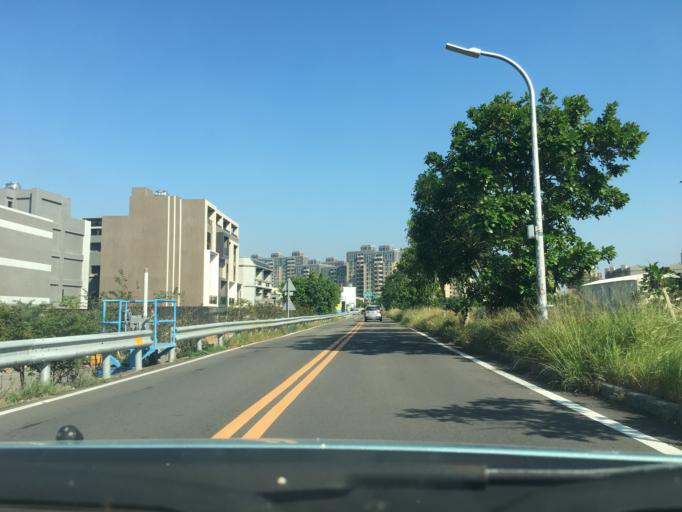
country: TW
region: Taiwan
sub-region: Hsinchu
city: Hsinchu
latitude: 24.8015
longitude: 120.9479
